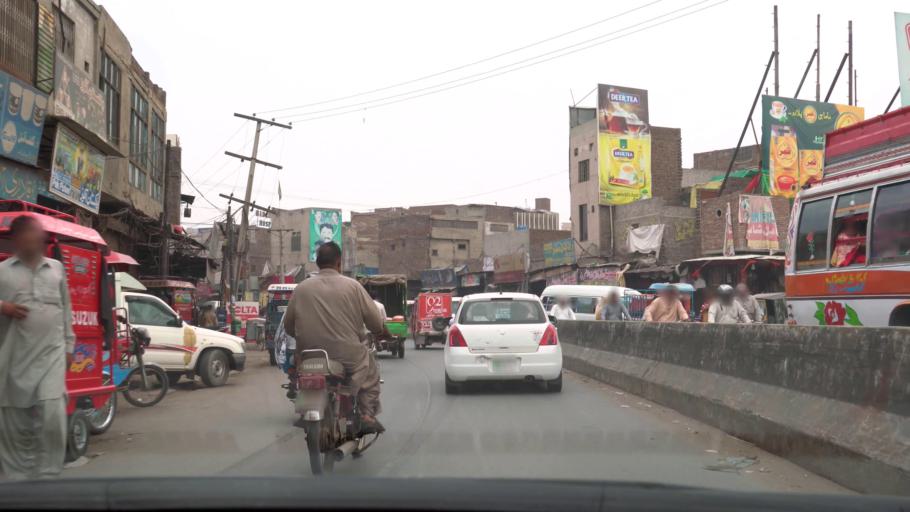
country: PK
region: Punjab
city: Faisalabad
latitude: 31.4314
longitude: 73.0935
